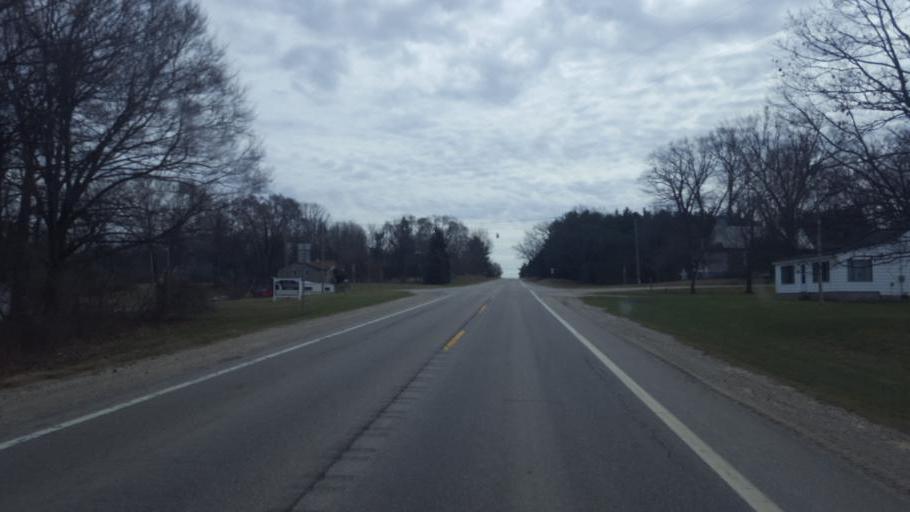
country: US
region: Michigan
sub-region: Isabella County
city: Lake Isabella
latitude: 43.6836
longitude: -85.1465
